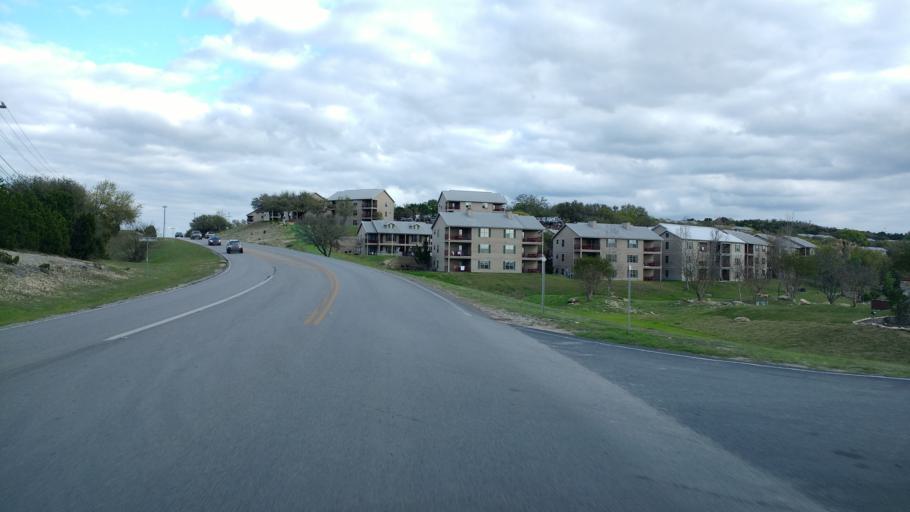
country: US
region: Texas
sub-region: Comal County
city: Canyon Lake
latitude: 29.9110
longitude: -98.2128
